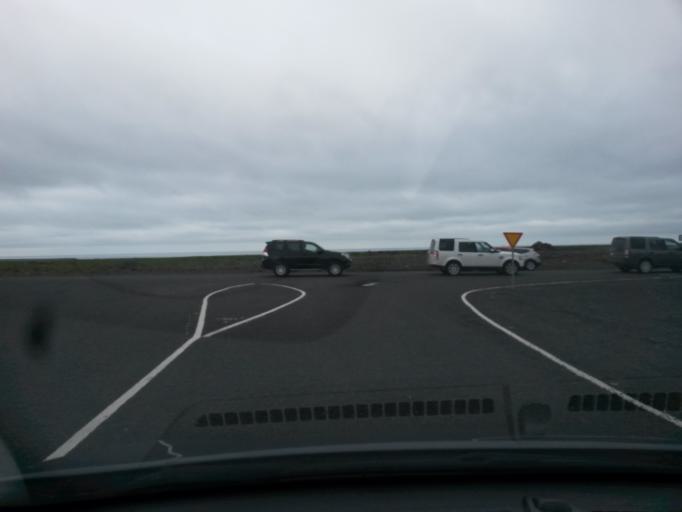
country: IS
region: South
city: Vestmannaeyjar
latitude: 63.4983
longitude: -19.3975
